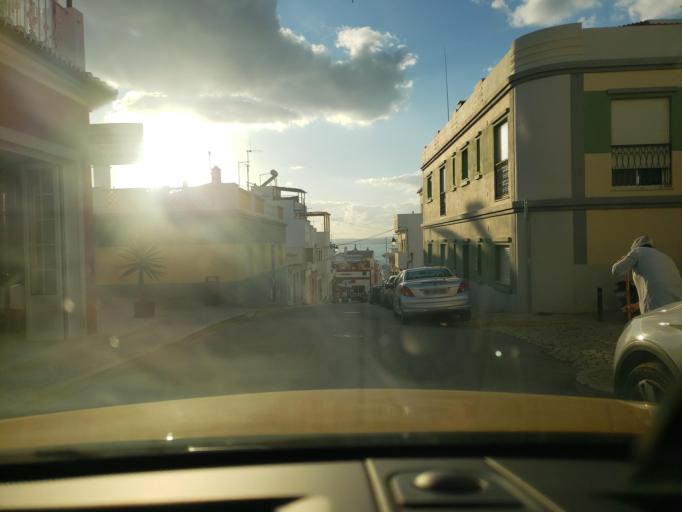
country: PT
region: Faro
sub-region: Portimao
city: Alvor
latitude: 37.1309
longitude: -8.5947
